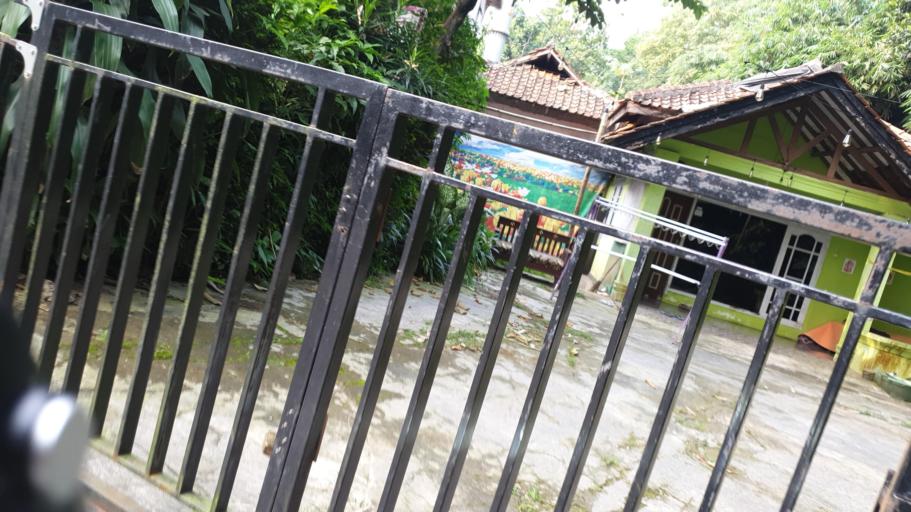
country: ID
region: West Java
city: Depok
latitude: -6.3684
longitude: 106.8409
